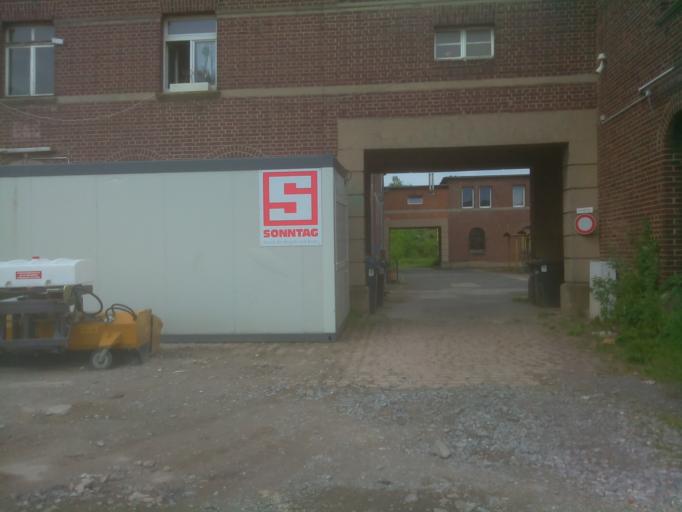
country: DE
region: Baden-Wuerttemberg
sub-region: Karlsruhe Region
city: Eppelheim
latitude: 49.4086
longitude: 8.6521
